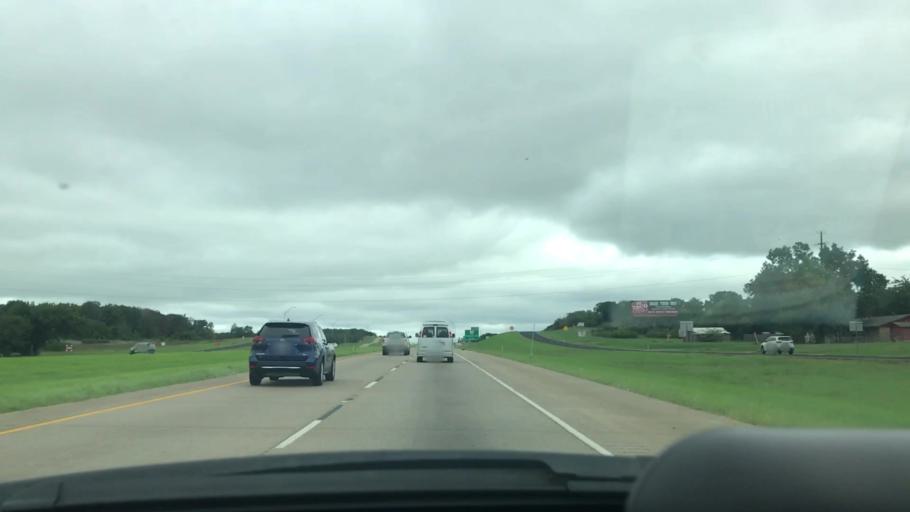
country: US
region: Texas
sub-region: Grayson County
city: Denison
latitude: 33.7400
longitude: -96.5852
